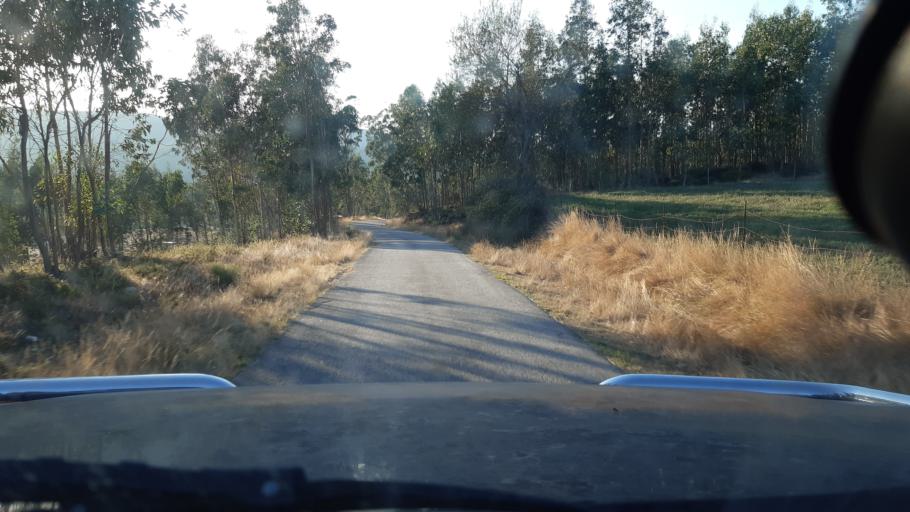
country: PT
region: Viseu
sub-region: Mortagua
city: Mortagua
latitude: 40.5449
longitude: -8.2581
